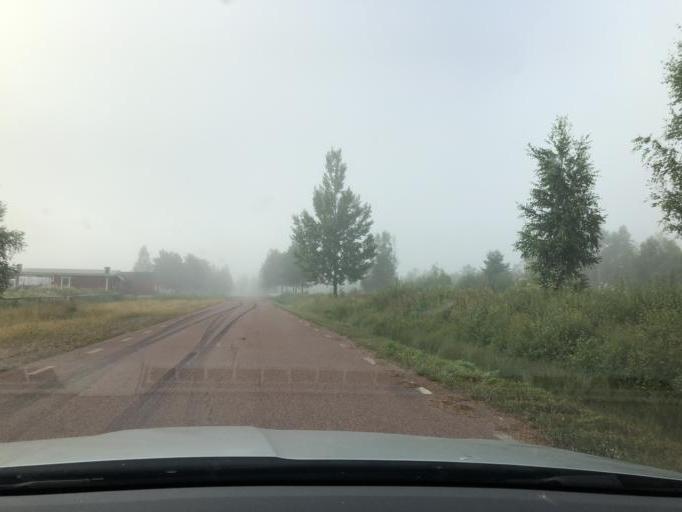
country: SE
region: Dalarna
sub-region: Mora Kommun
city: Mora
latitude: 60.9635
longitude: 14.4998
